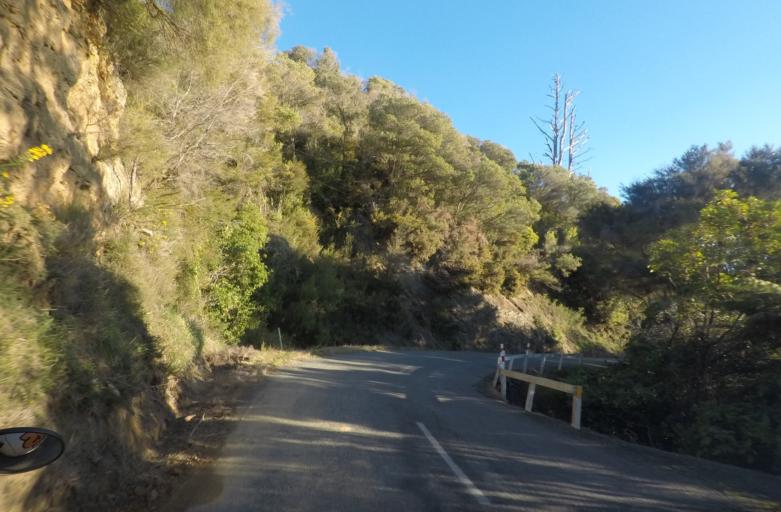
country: NZ
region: Marlborough
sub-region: Marlborough District
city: Picton
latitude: -41.2686
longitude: 173.9554
